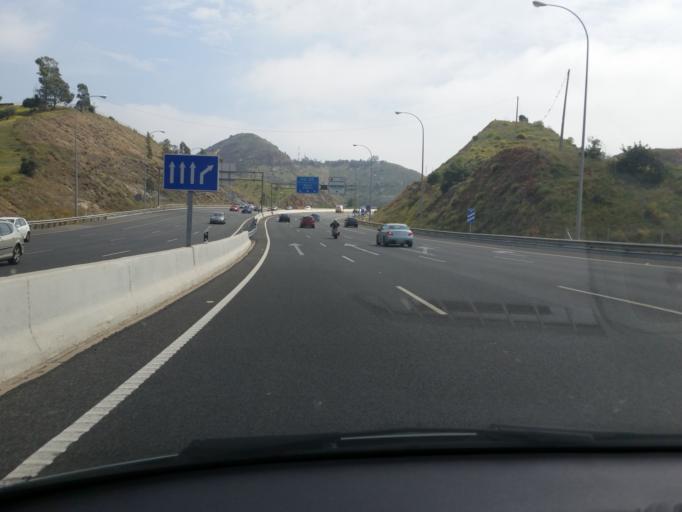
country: ES
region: Andalusia
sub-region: Provincia de Malaga
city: Malaga
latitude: 36.7398
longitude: -4.3992
